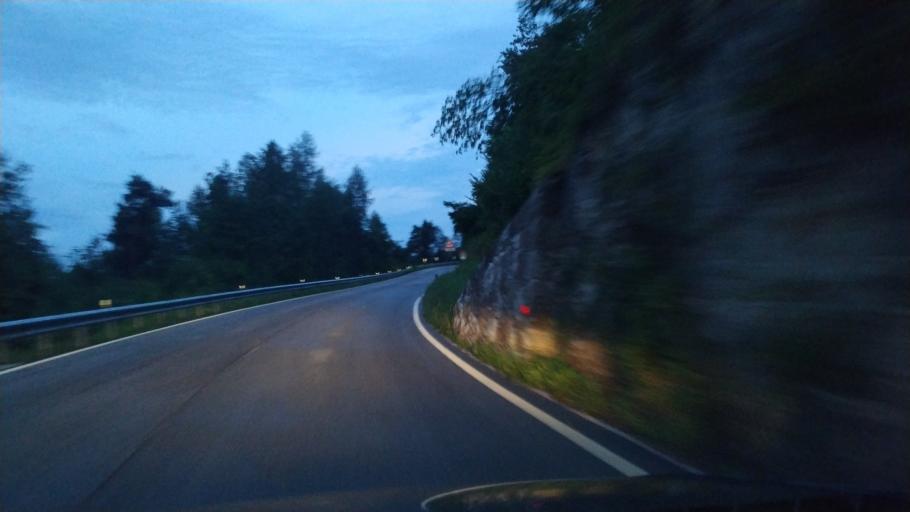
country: IT
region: Trentino-Alto Adige
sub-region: Provincia di Trento
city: Cagno
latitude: 46.3857
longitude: 11.0378
